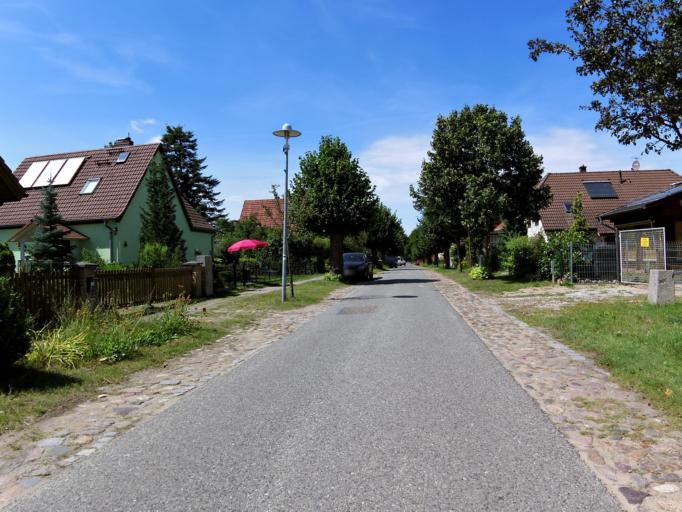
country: DE
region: Brandenburg
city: Furstenberg
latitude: 53.1794
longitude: 13.2231
